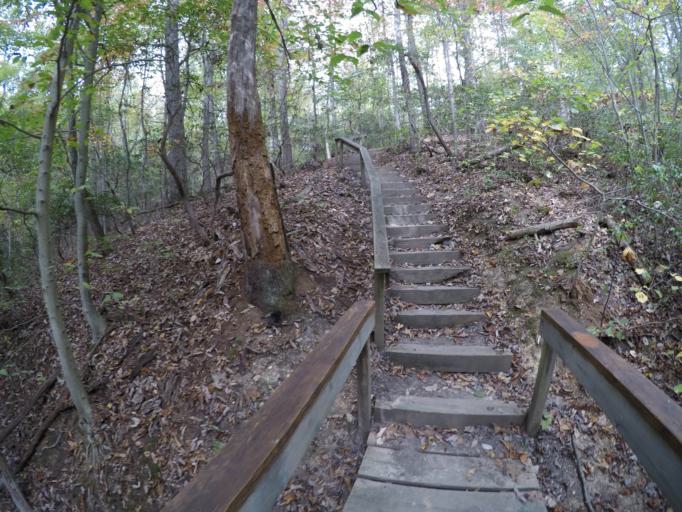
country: US
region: Maryland
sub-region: Harford County
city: Riverside
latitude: 39.4513
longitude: -76.2694
